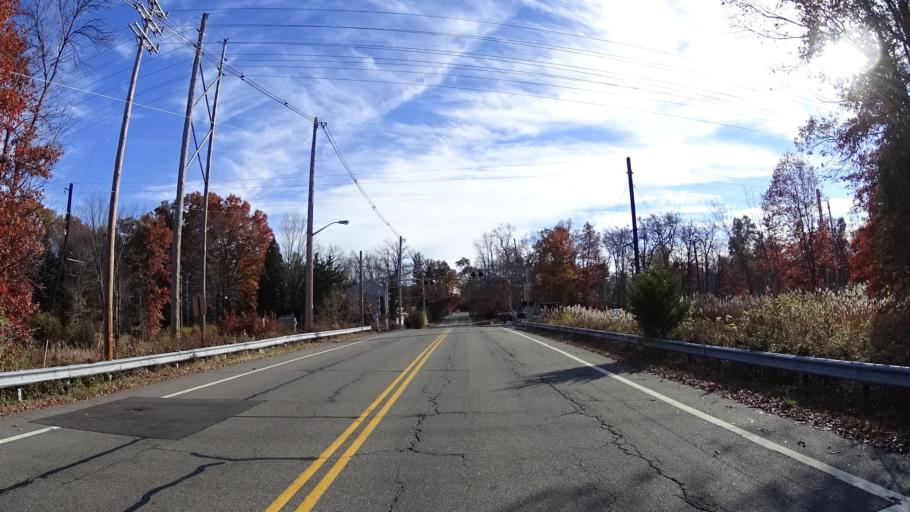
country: US
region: New Jersey
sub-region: Union County
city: Berkeley Heights
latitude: 40.6791
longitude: -74.4679
